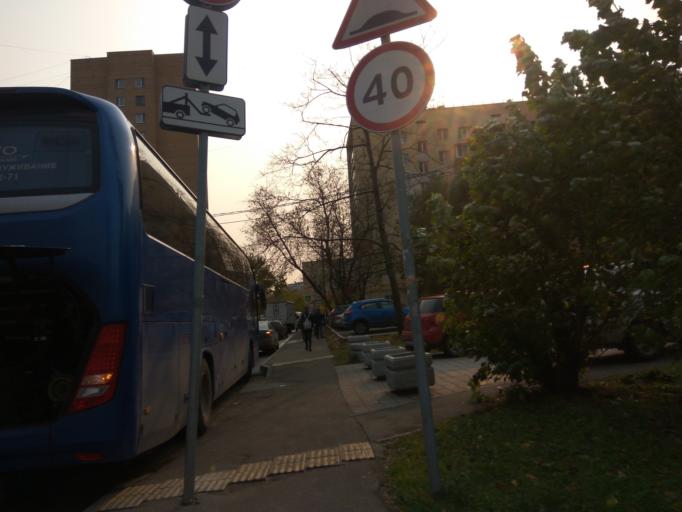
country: RU
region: Moskovskaya
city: Bogorodskoye
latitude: 55.7981
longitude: 37.7178
